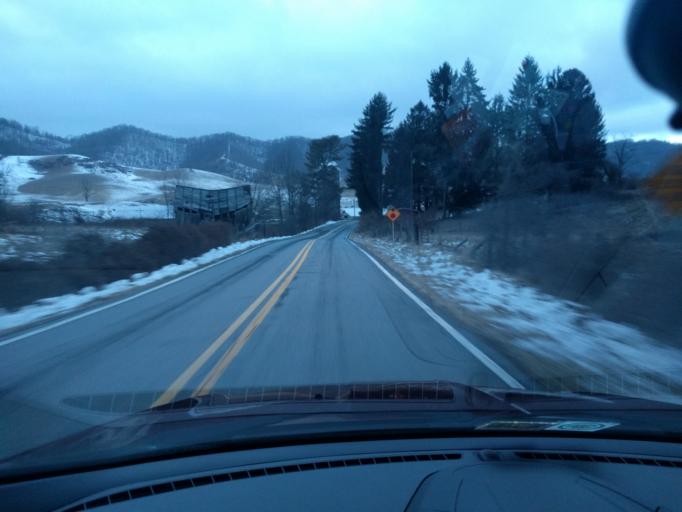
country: US
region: Virginia
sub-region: Alleghany County
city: Clifton Forge
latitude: 37.9039
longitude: -79.8974
